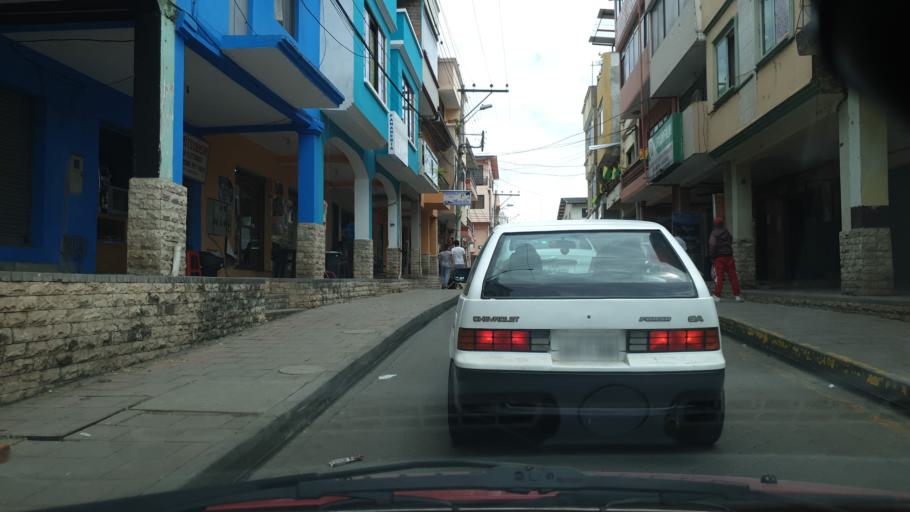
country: EC
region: Azuay
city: Cuenca
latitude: -3.2735
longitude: -79.3153
